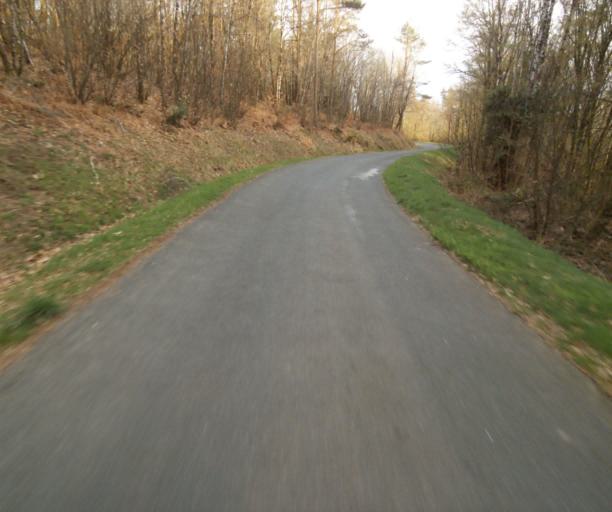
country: FR
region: Limousin
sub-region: Departement de la Correze
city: Argentat
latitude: 45.2413
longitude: 1.9643
